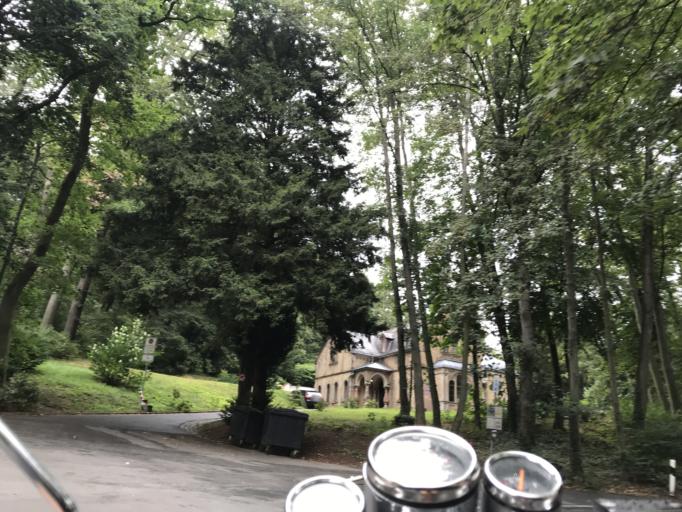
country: DE
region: Hesse
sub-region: Regierungsbezirk Darmstadt
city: Wiesbaden
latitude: 50.0976
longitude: 8.2354
